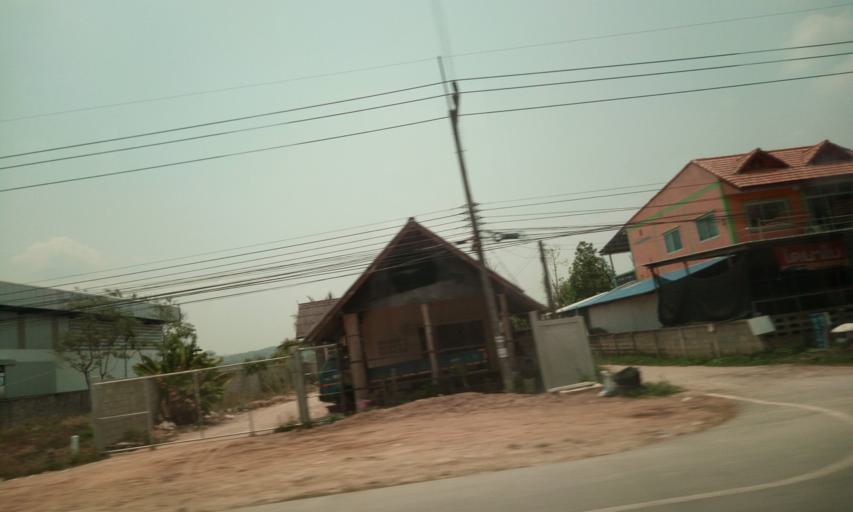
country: TH
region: Chiang Rai
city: Thoeng
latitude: 19.6828
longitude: 100.1292
